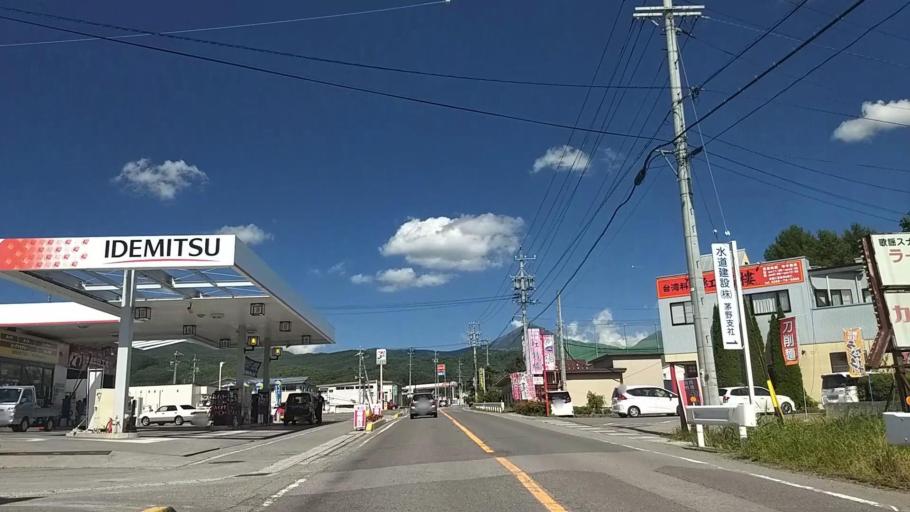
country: JP
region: Nagano
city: Chino
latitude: 36.0284
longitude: 138.1837
